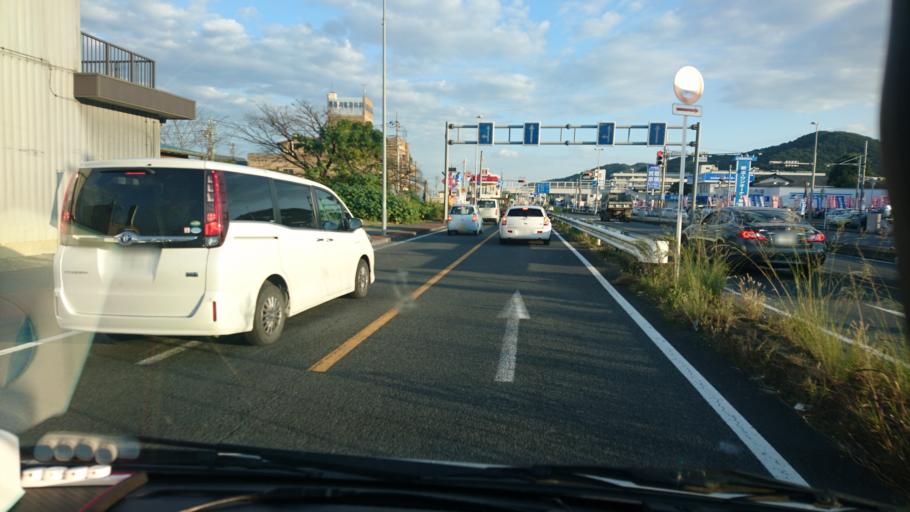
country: JP
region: Gunma
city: Kiryu
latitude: 36.3828
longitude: 139.3393
